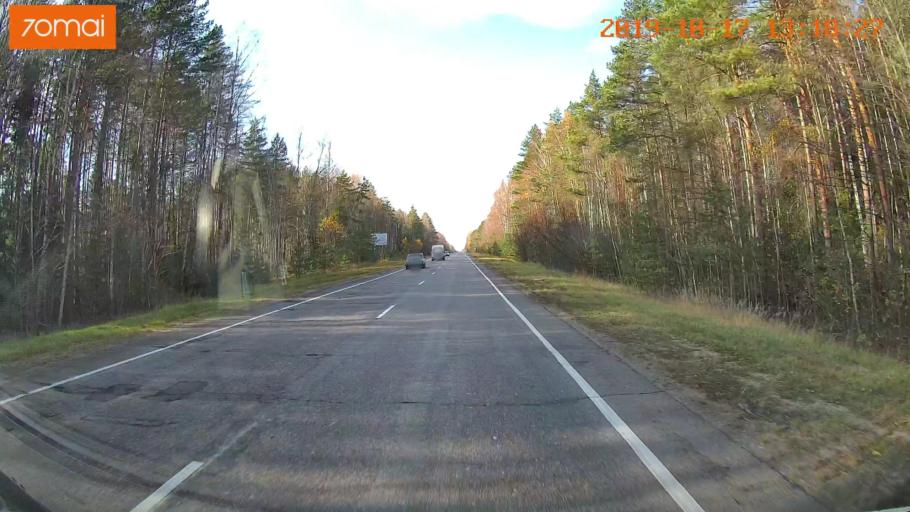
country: RU
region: Rjazan
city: Gus'-Zheleznyy
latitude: 55.0630
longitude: 41.0976
